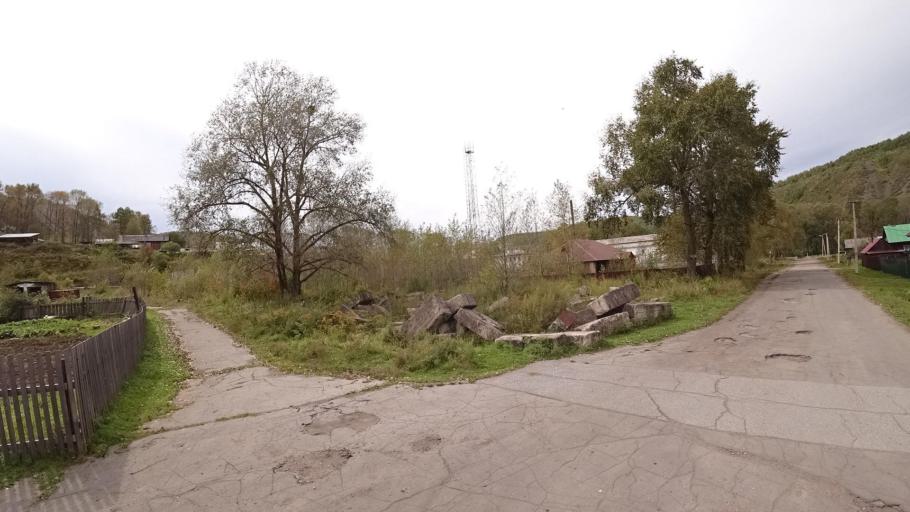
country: RU
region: Jewish Autonomous Oblast
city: Khingansk
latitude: 49.1264
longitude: 131.1972
